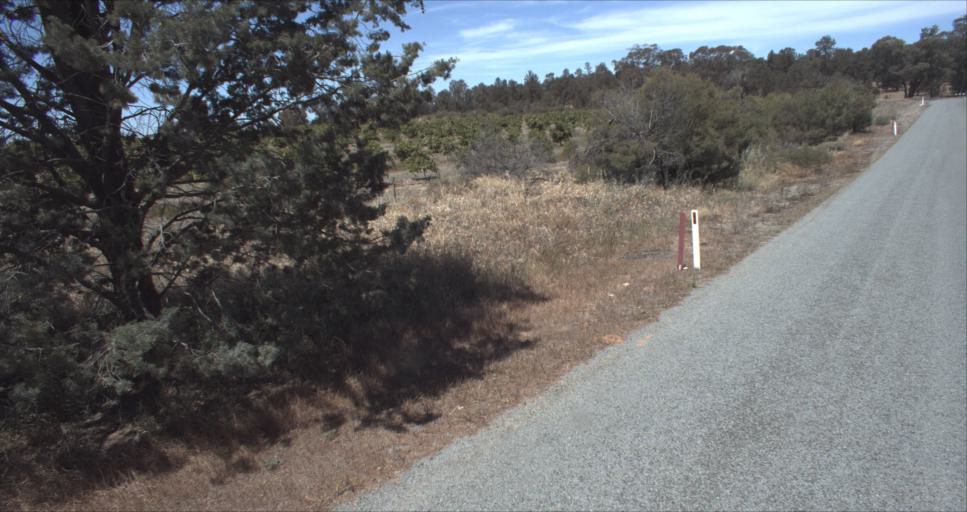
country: AU
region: New South Wales
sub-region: Leeton
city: Leeton
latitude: -34.6680
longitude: 146.4467
